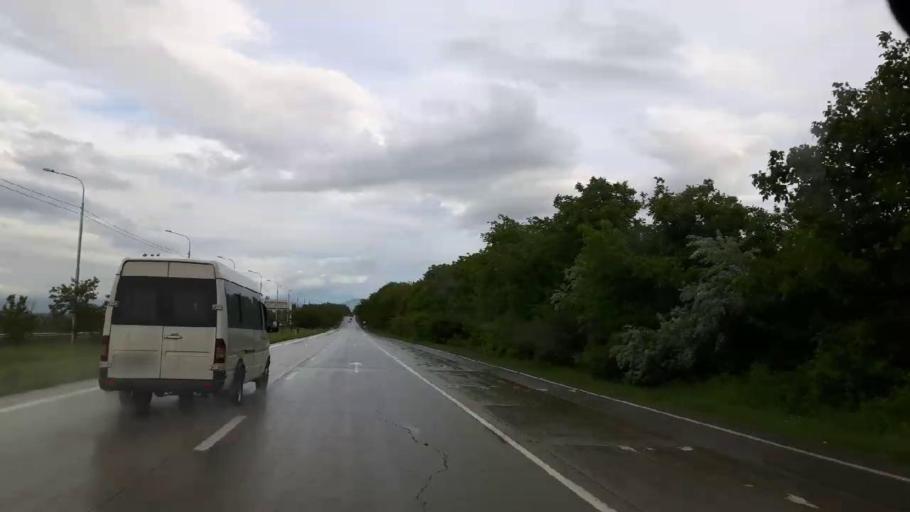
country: GE
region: Shida Kartli
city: Kaspi
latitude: 41.9615
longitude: 44.4762
